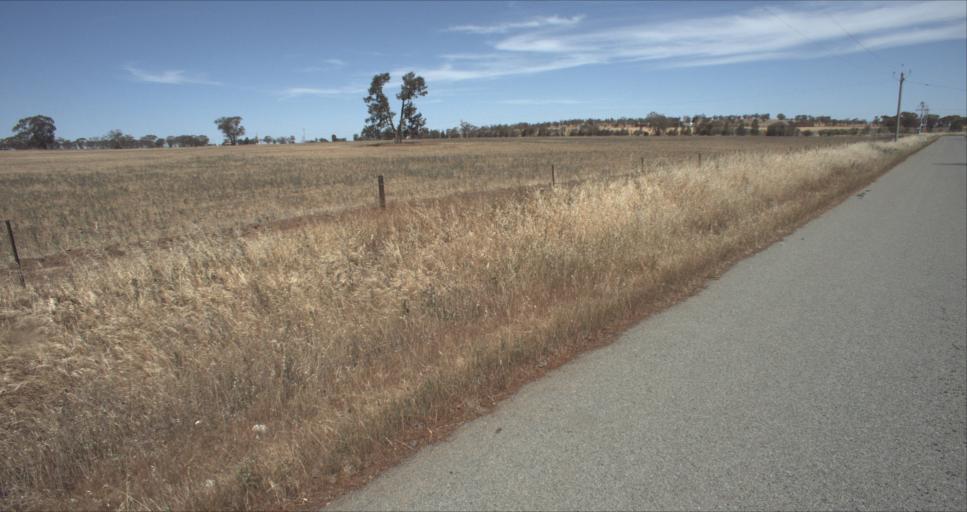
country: AU
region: New South Wales
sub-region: Leeton
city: Leeton
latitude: -34.6125
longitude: 146.4342
